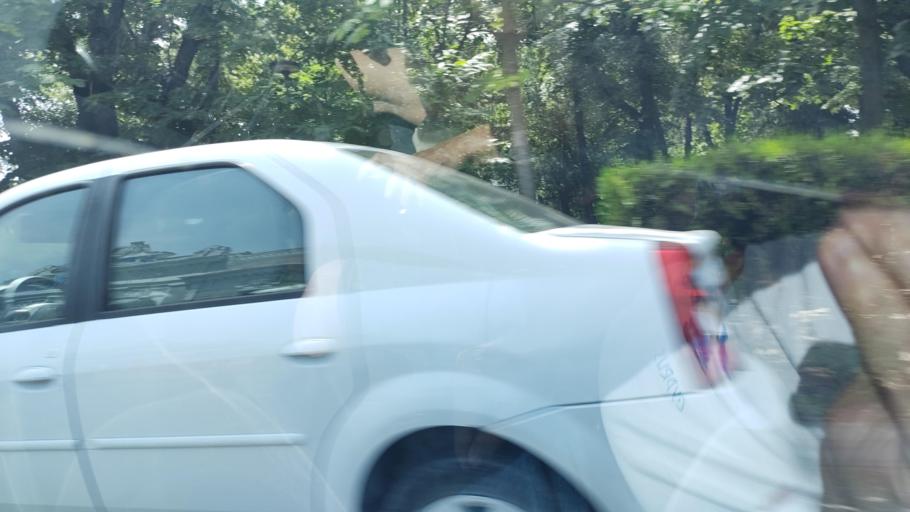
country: RO
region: Mehedinti
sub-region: Municipiul Drobeta-Turnu Severin
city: Drobeta-Turnu Severin
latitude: 44.6244
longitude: 22.6567
